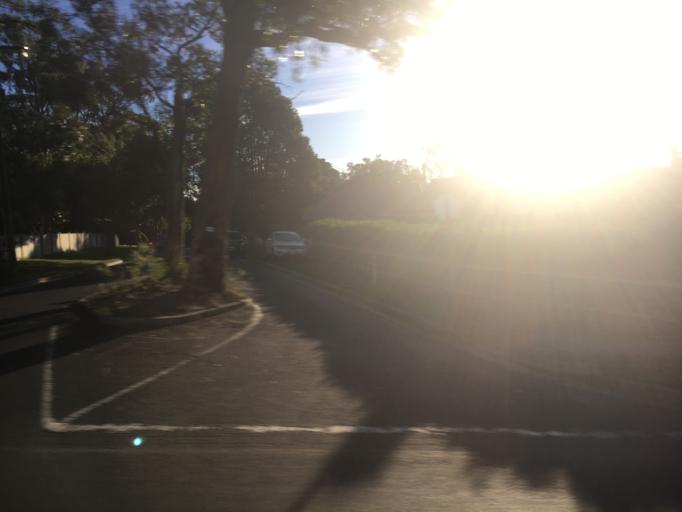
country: AU
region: Victoria
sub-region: Yarra Ranges
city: Tecoma
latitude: -37.9132
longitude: 145.3386
